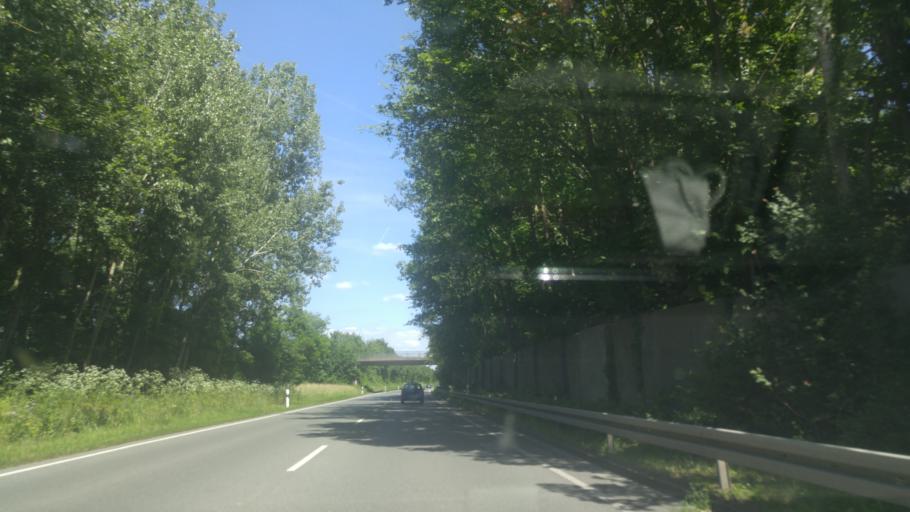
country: DE
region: Bavaria
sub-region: Regierungsbezirk Mittelfranken
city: Erlangen
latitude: 49.5725
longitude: 10.9571
